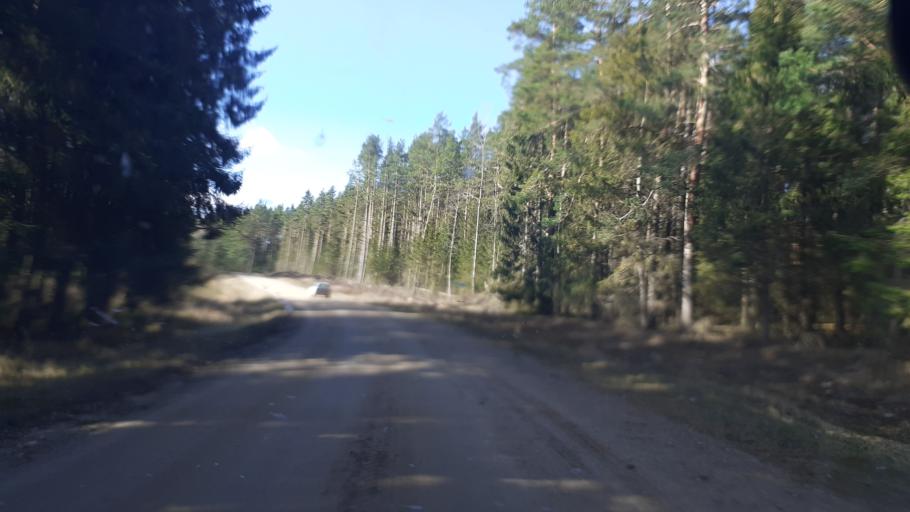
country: LV
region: Kuldigas Rajons
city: Kuldiga
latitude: 56.9126
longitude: 22.0904
